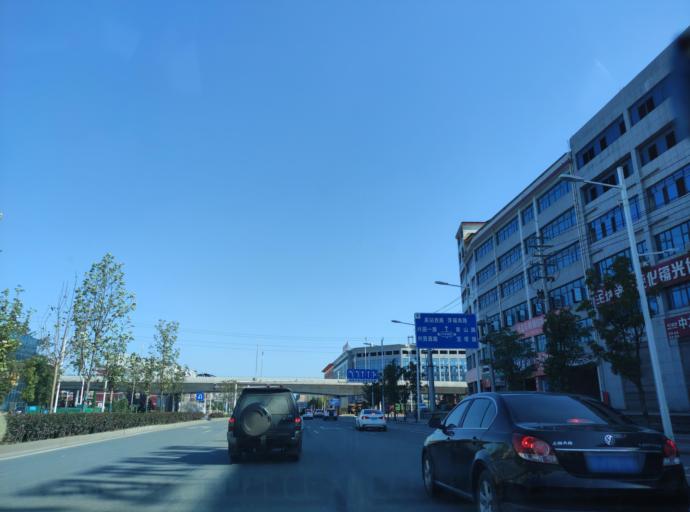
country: CN
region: Jiangxi Sheng
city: Pingxiang
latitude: 27.6620
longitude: 113.8228
